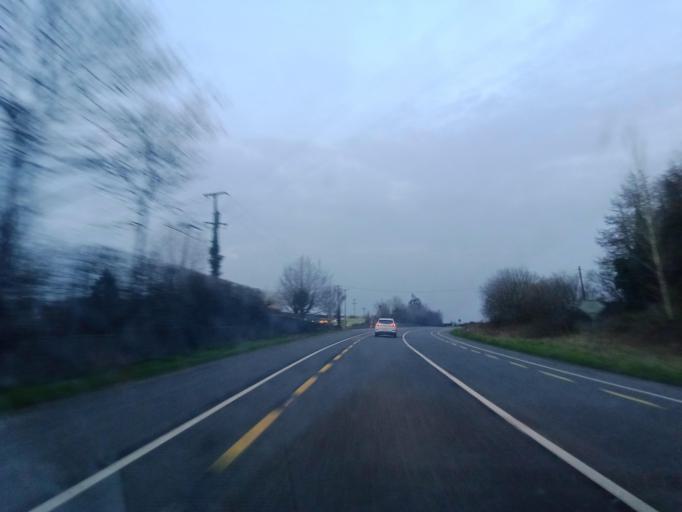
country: IE
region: Leinster
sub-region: Laois
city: Abbeyleix
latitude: 52.8579
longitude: -7.3827
